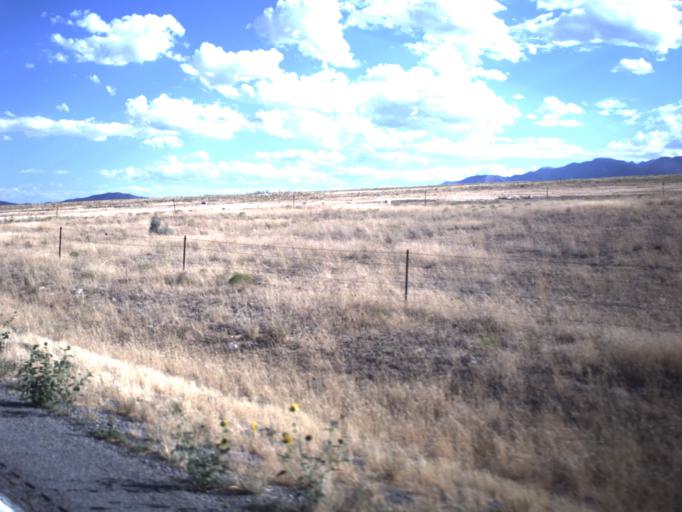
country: US
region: Utah
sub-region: Tooele County
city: Grantsville
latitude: 40.6344
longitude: -112.5174
